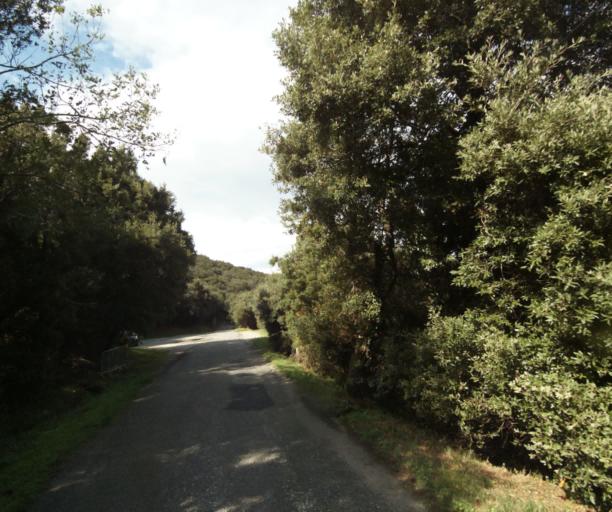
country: FR
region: Languedoc-Roussillon
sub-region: Departement des Pyrenees-Orientales
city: Sorede
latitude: 42.5144
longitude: 2.9886
